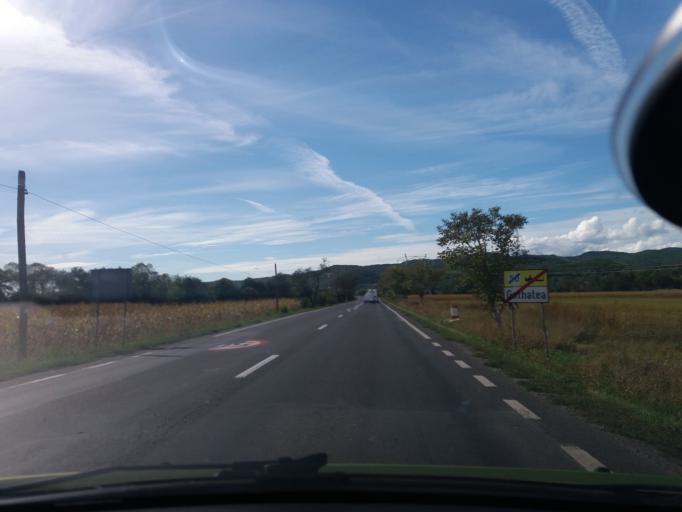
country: RO
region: Hunedoara
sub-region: Comuna Dobra
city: Dobra
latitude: 45.9466
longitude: 22.6004
